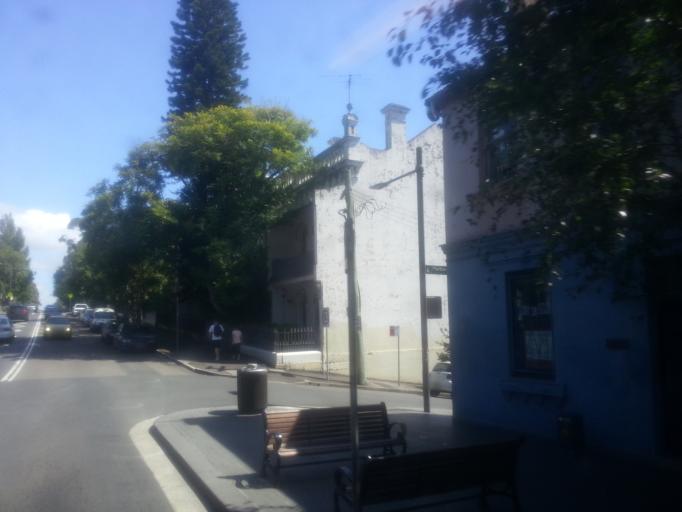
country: AU
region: New South Wales
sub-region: City of Sydney
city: Chippendale
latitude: -33.8791
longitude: 151.1865
